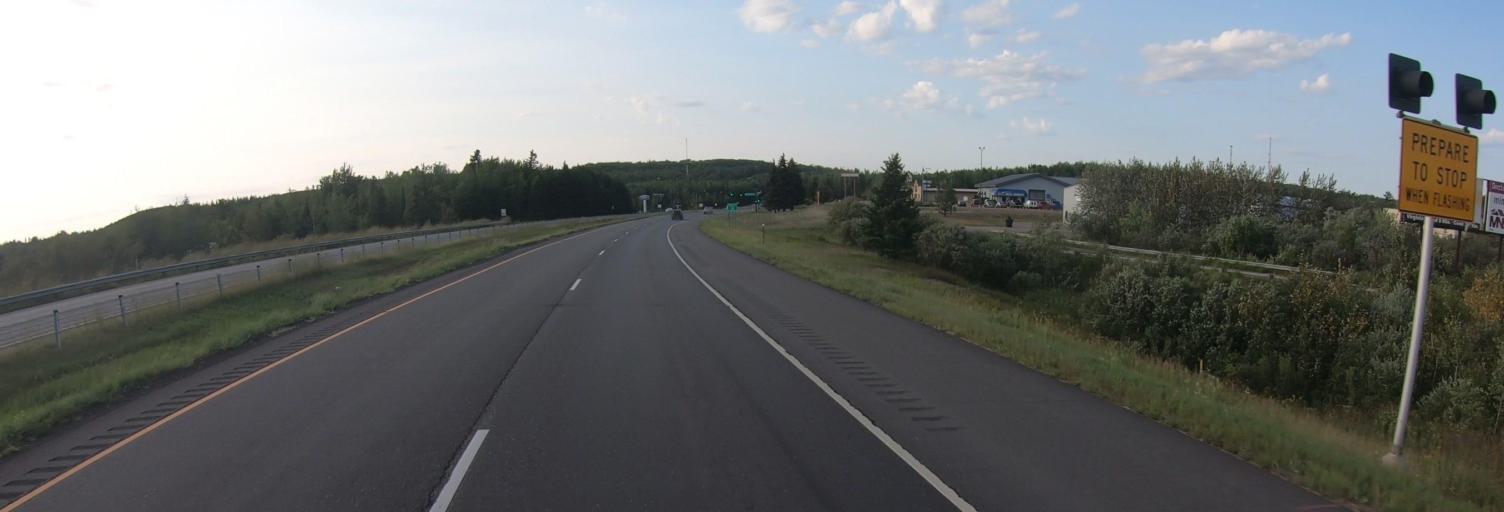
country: US
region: Minnesota
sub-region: Saint Louis County
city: Eveleth
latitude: 47.4747
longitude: -92.5293
